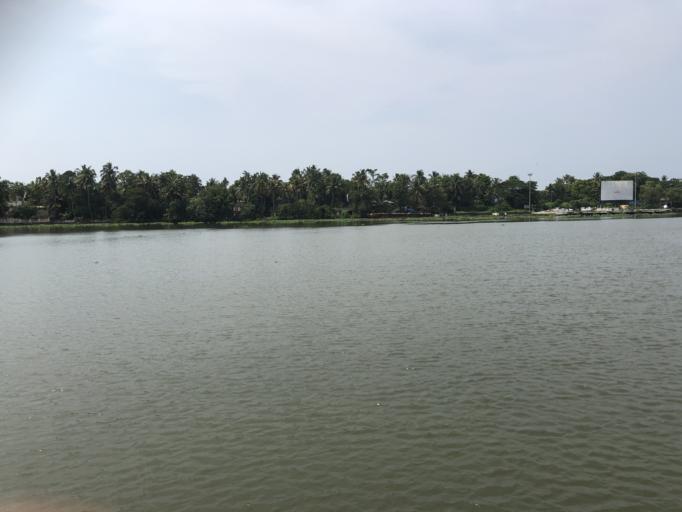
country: IN
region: Kerala
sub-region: Ernakulam
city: Cochin
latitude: 9.9899
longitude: 76.2688
